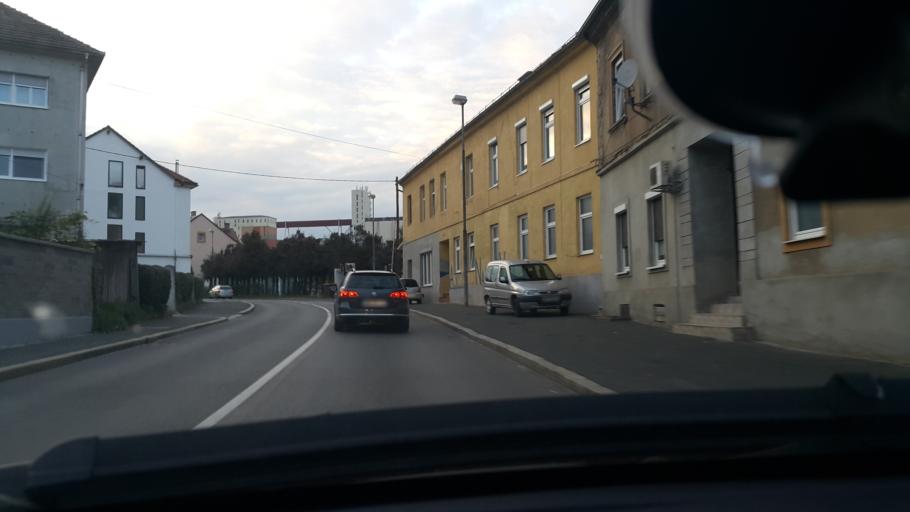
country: SI
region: Maribor
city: Maribor
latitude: 46.5604
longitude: 15.6659
